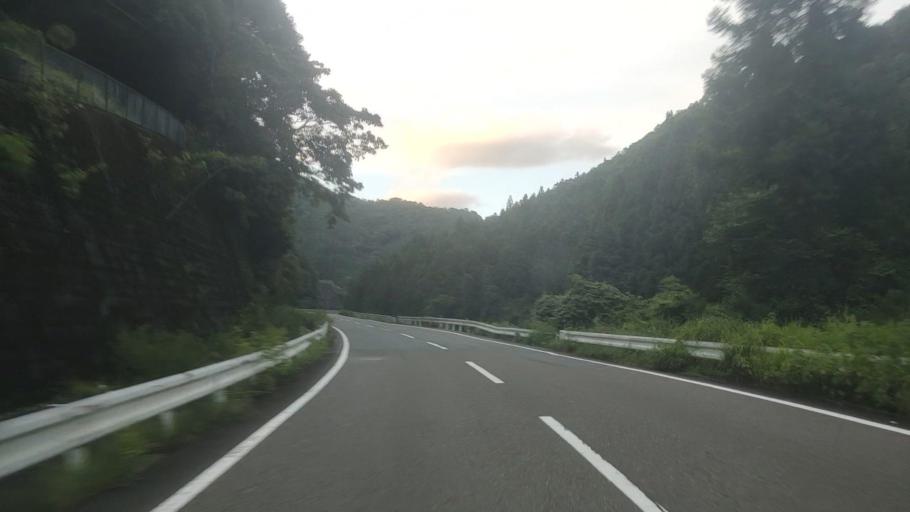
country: JP
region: Wakayama
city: Shingu
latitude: 33.8069
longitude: 135.7347
